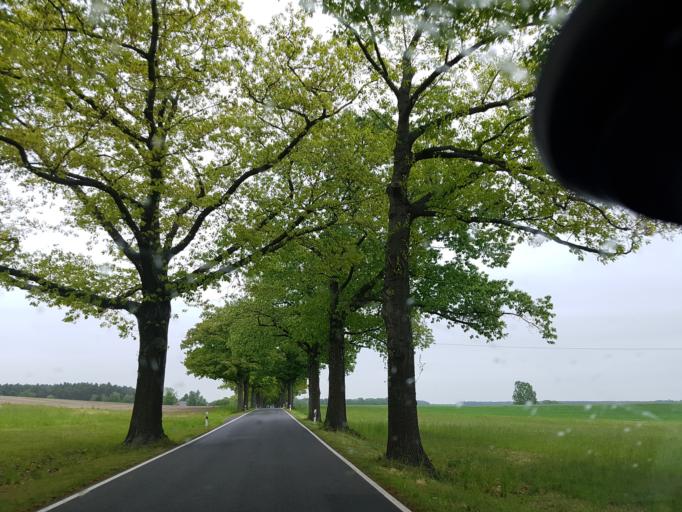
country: DE
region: Brandenburg
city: Spremberg
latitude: 51.6546
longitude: 14.3320
